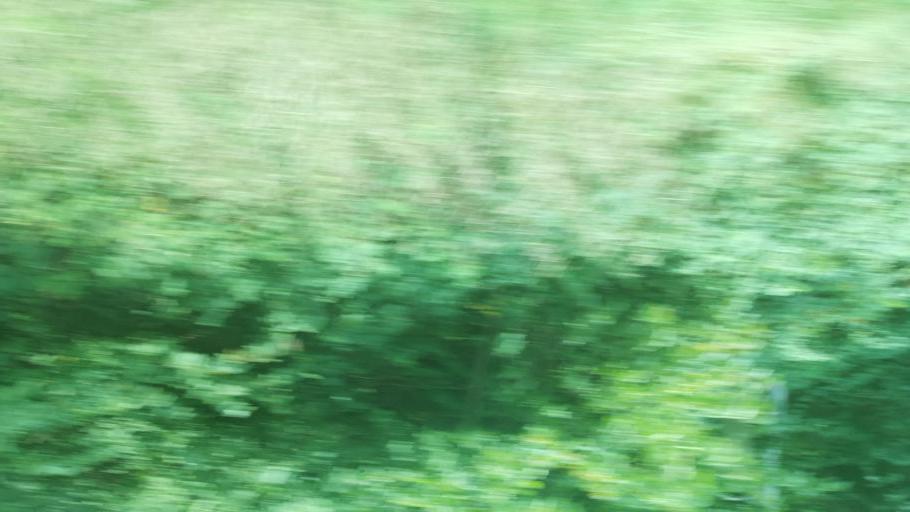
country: DE
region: Bavaria
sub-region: Upper Palatinate
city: Chamerau
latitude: 49.1885
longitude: 12.7324
